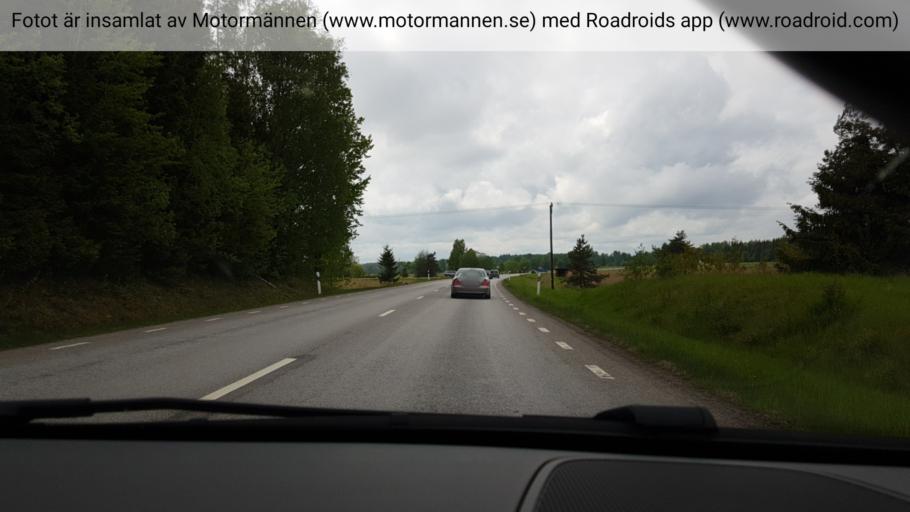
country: SE
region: Uppsala
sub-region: Osthammars Kommun
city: Osterbybruk
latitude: 60.1616
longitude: 17.9900
